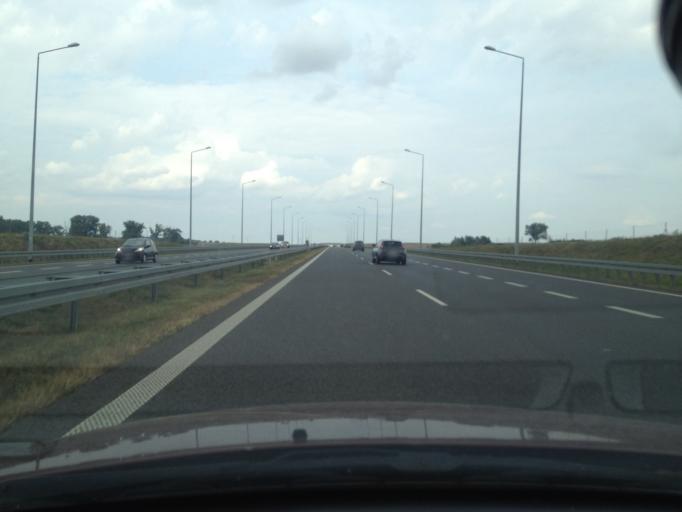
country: PL
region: West Pomeranian Voivodeship
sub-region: Powiat pyrzycki
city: Kozielice
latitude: 53.0539
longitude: 14.8652
